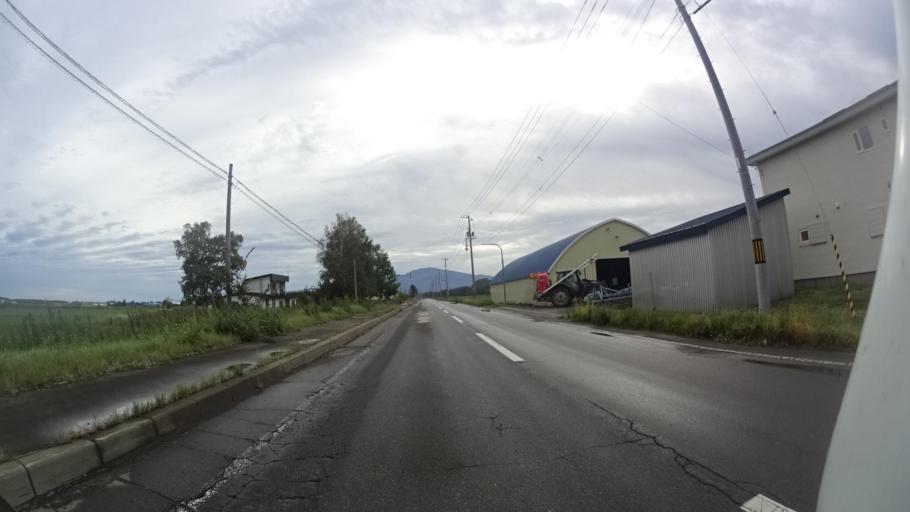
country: JP
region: Hokkaido
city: Abashiri
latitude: 43.8694
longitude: 144.6351
